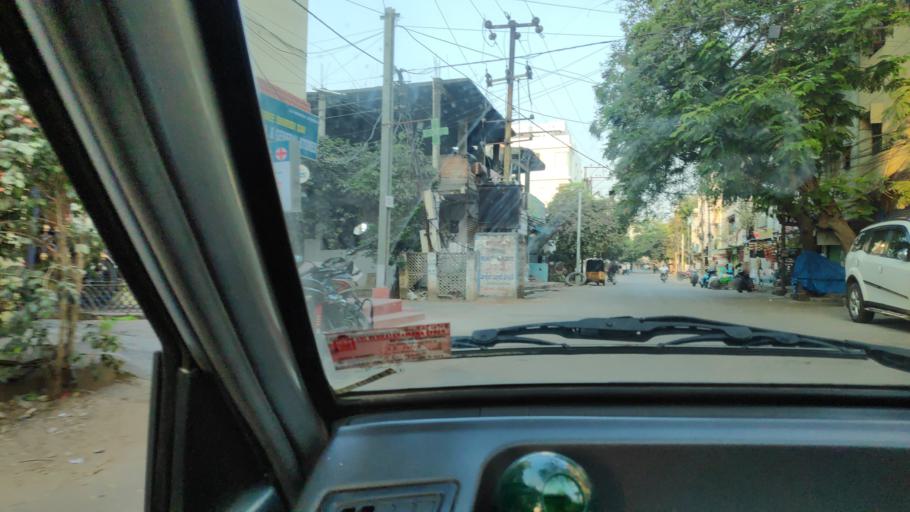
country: IN
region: Telangana
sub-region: Rangareddi
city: Gaddi Annaram
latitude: 17.3624
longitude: 78.5277
